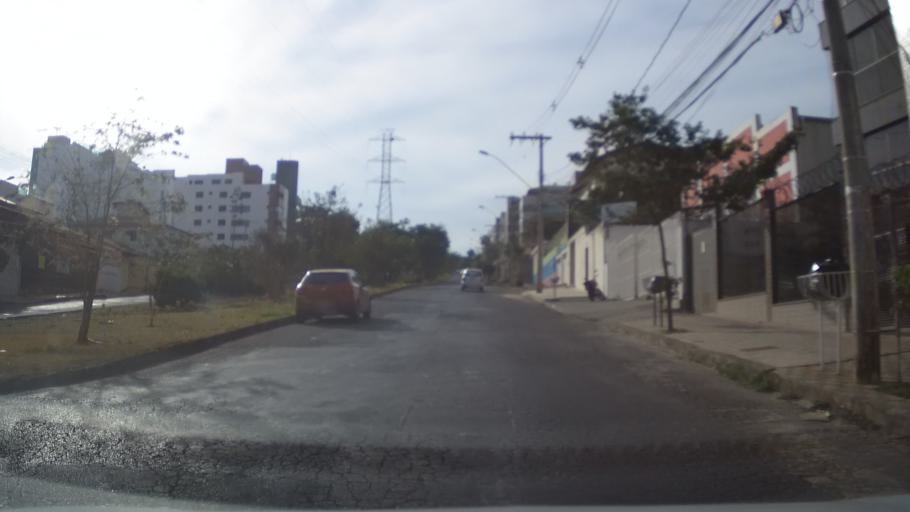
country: BR
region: Minas Gerais
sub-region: Contagem
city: Contagem
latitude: -19.8804
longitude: -44.0025
